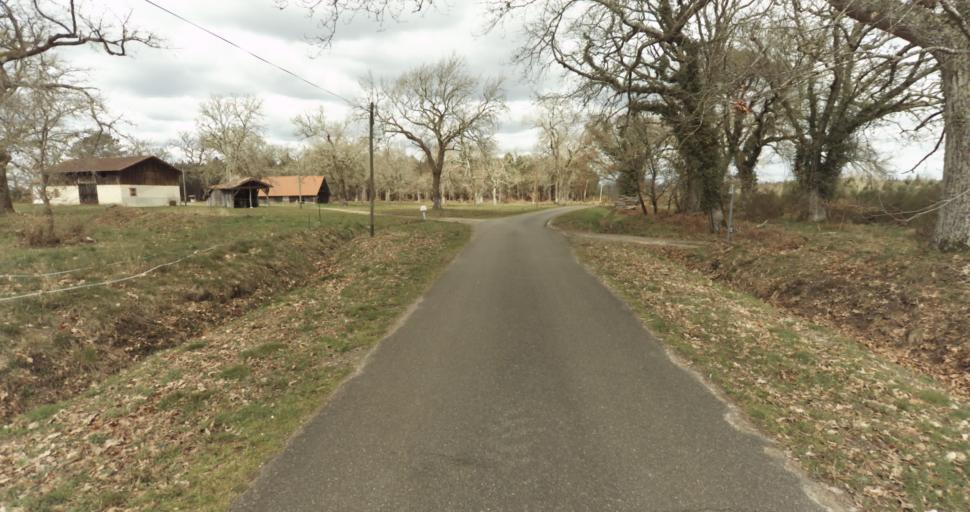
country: FR
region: Aquitaine
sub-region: Departement des Landes
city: Roquefort
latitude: 44.0908
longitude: -0.4545
